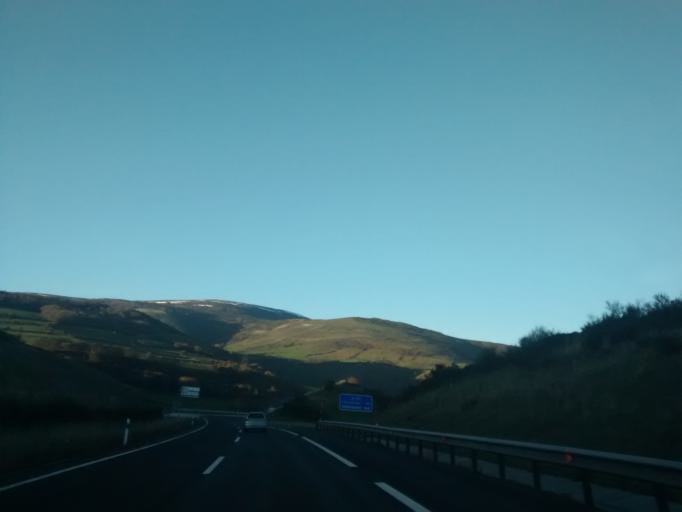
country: ES
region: Cantabria
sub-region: Provincia de Cantabria
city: Reinosa
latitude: 43.0137
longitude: -4.1235
